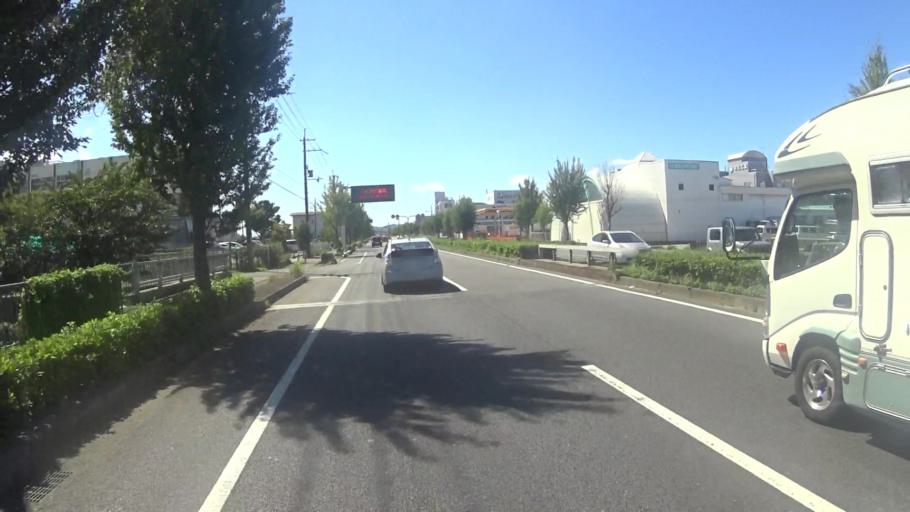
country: JP
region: Kyoto
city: Tanabe
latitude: 34.8639
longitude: 135.7625
